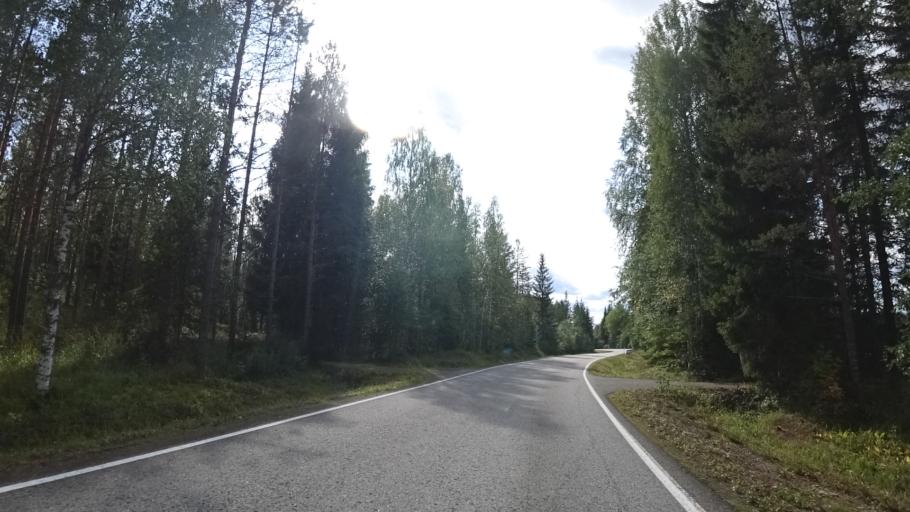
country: RU
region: Republic of Karelia
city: Vyartsilya
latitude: 62.2621
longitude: 30.7727
